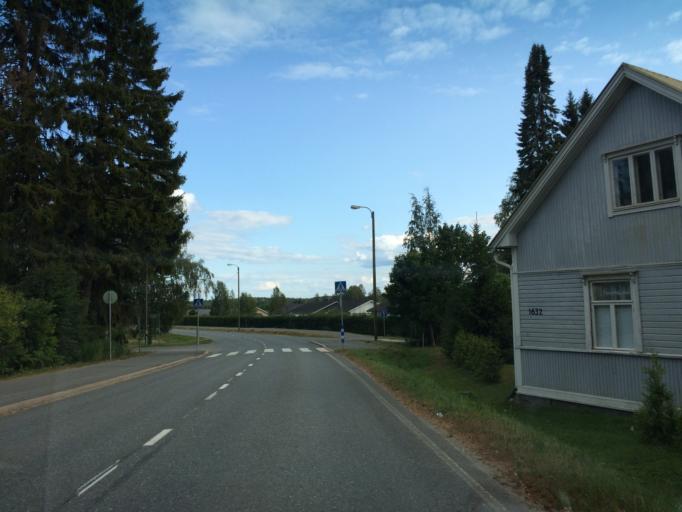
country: FI
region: Haeme
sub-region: Haemeenlinna
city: Tuulos
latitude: 61.0694
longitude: 24.6800
